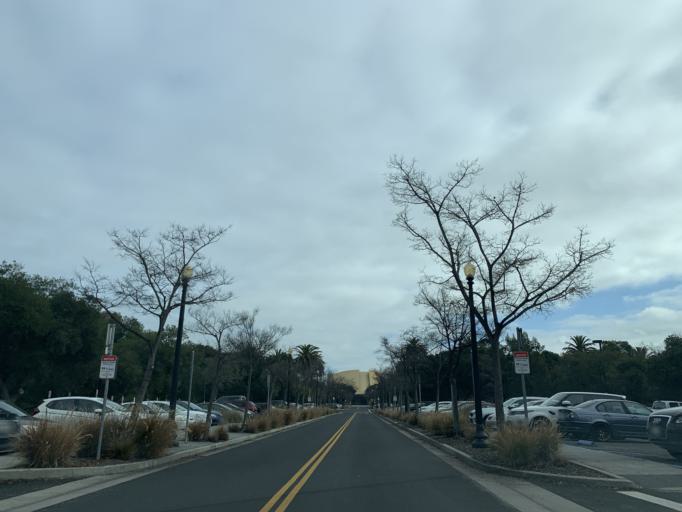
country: US
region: California
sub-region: Santa Clara County
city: Stanford
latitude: 37.4329
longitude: -122.1701
